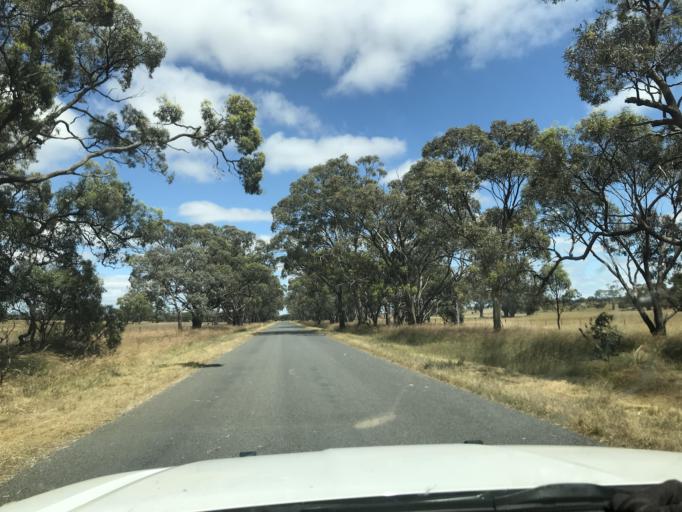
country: AU
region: South Australia
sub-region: Tatiara
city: Bordertown
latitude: -36.3107
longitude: 141.0287
